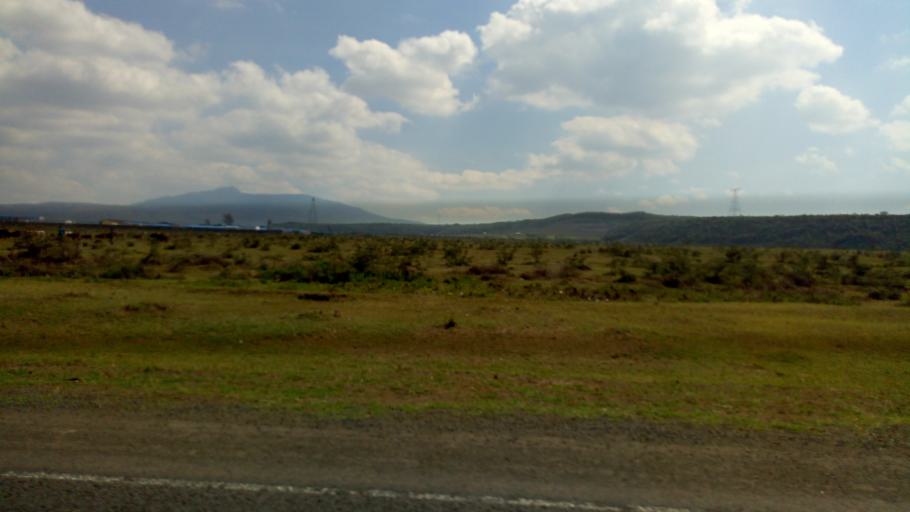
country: KE
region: Nakuru
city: Kijabe
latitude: -1.0119
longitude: 36.4950
